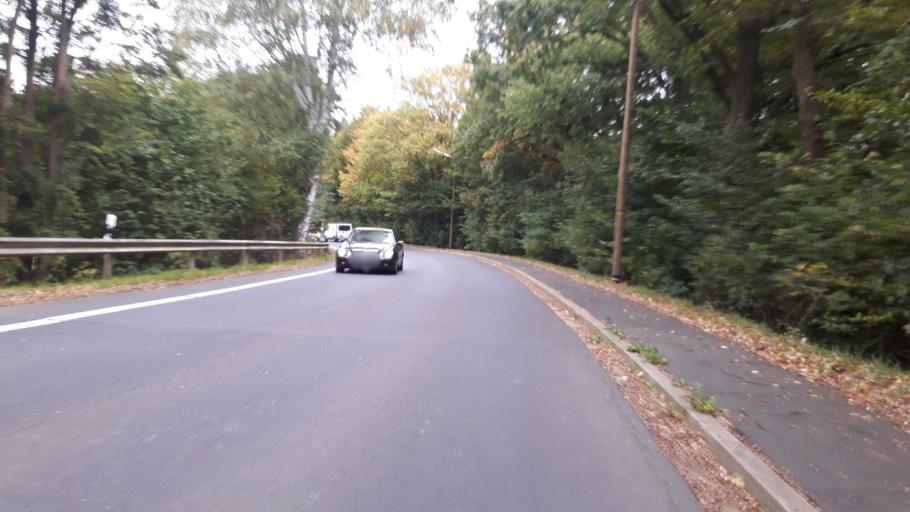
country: DE
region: North Rhine-Westphalia
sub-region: Regierungsbezirk Koln
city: Hennef
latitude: 50.7723
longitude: 7.3491
